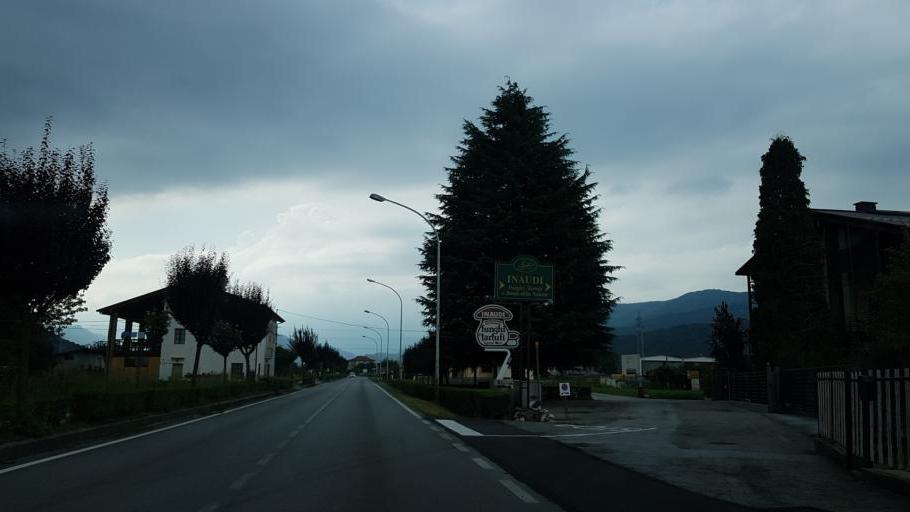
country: IT
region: Piedmont
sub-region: Provincia di Cuneo
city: Roccavione
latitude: 44.3332
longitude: 7.4713
